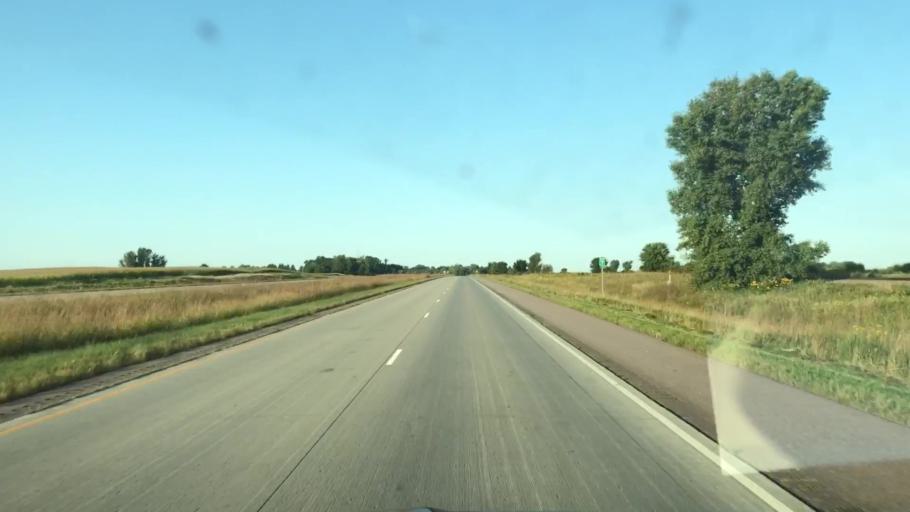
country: US
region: Minnesota
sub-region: Nobles County
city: Worthington
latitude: 43.5916
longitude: -95.6376
